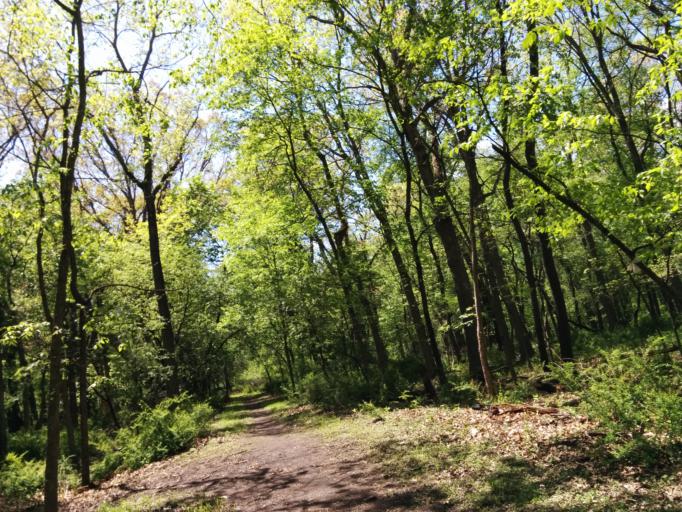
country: US
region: Illinois
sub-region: Cook County
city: Schiller Park
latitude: 41.9684
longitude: -87.8512
